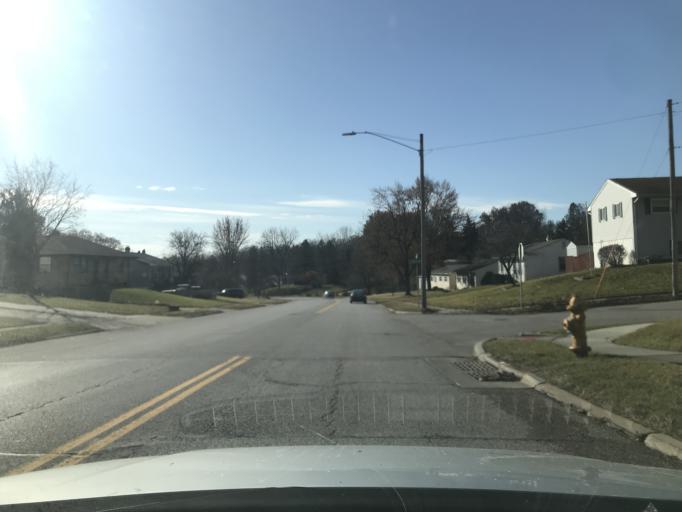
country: US
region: Iowa
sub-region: Scott County
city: Davenport
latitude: 41.5293
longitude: -90.6152
